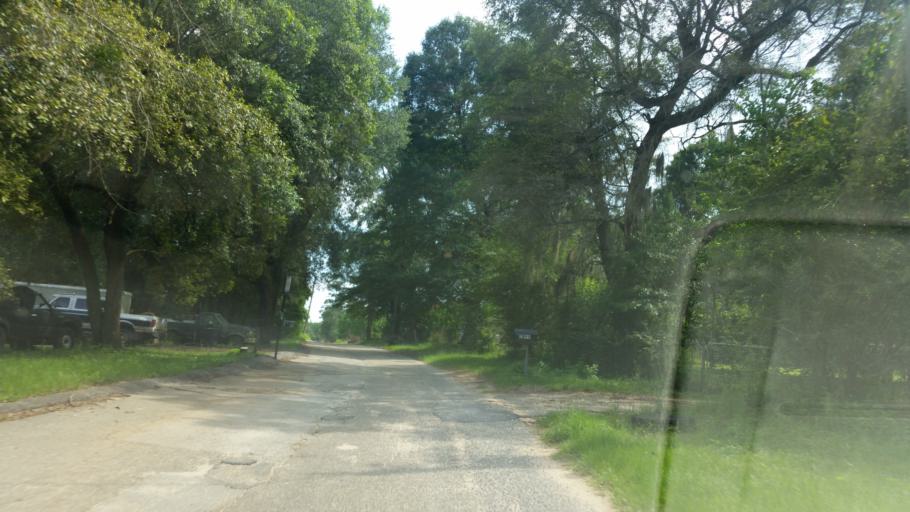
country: US
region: Florida
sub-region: Escambia County
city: Cantonment
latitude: 30.6282
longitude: -87.3828
